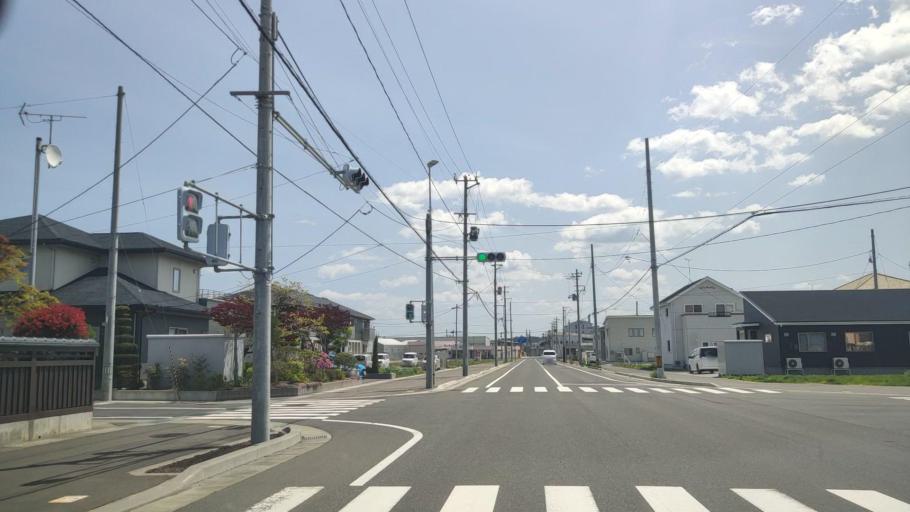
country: JP
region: Aomori
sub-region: Hachinohe Shi
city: Uchimaru
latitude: 40.5148
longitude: 141.4313
